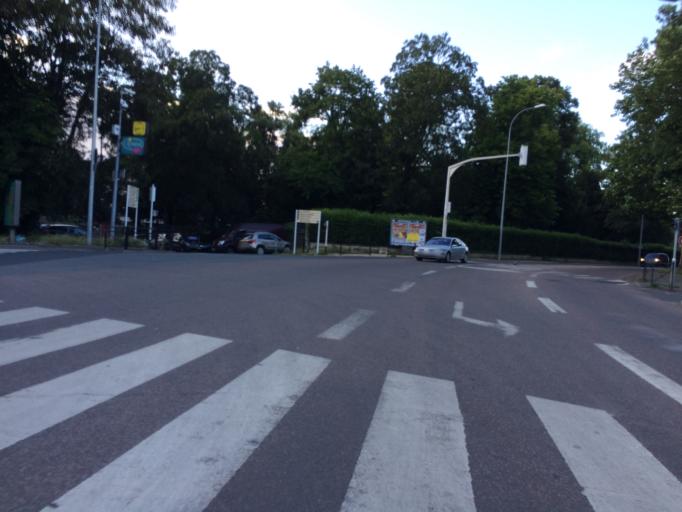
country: FR
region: Ile-de-France
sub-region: Departement de l'Essonne
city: Draveil
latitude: 48.6873
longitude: 2.4332
